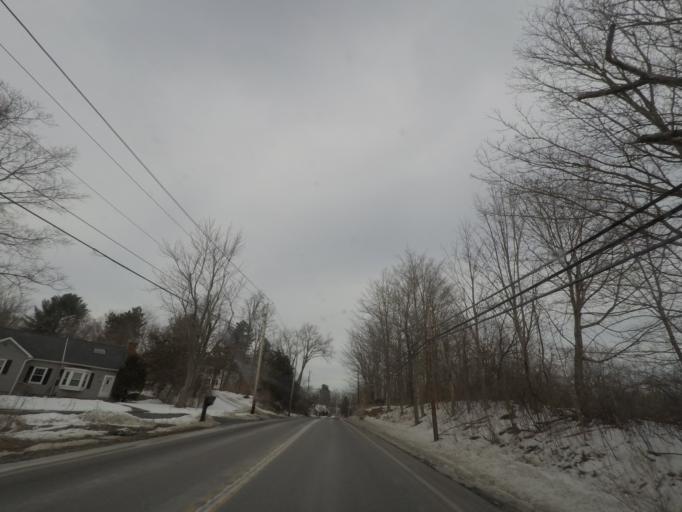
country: US
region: New York
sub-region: Albany County
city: Voorheesville
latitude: 42.5889
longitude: -73.9149
